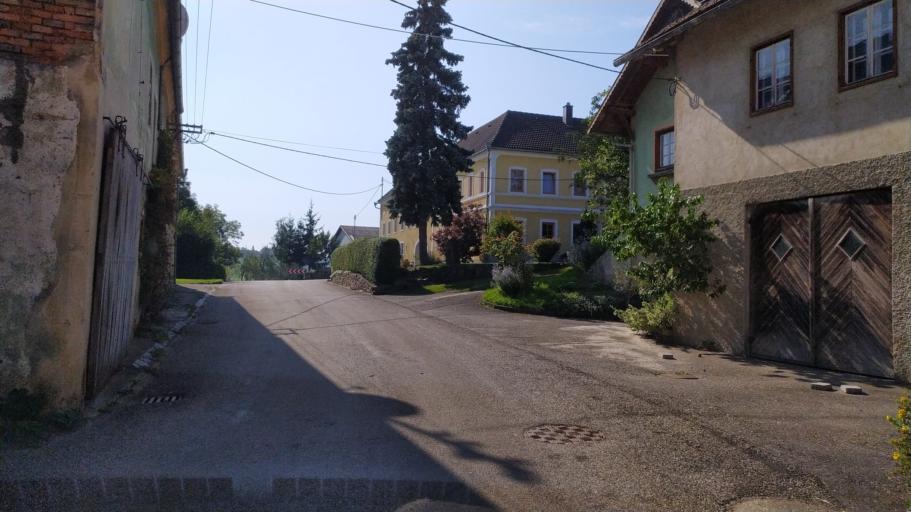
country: AT
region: Lower Austria
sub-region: Politischer Bezirk Amstetten
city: Zeillern
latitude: 48.1072
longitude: 14.7473
